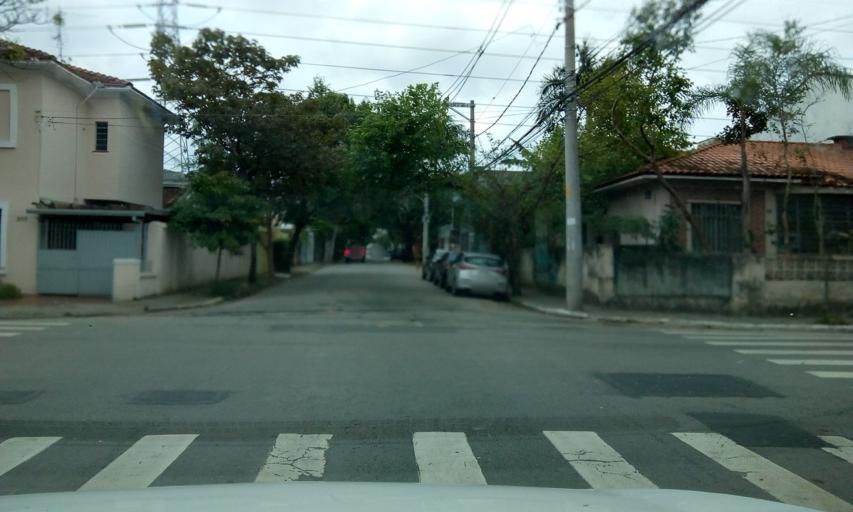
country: BR
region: Sao Paulo
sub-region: Sao Paulo
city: Sao Paulo
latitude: -23.6071
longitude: -46.6825
